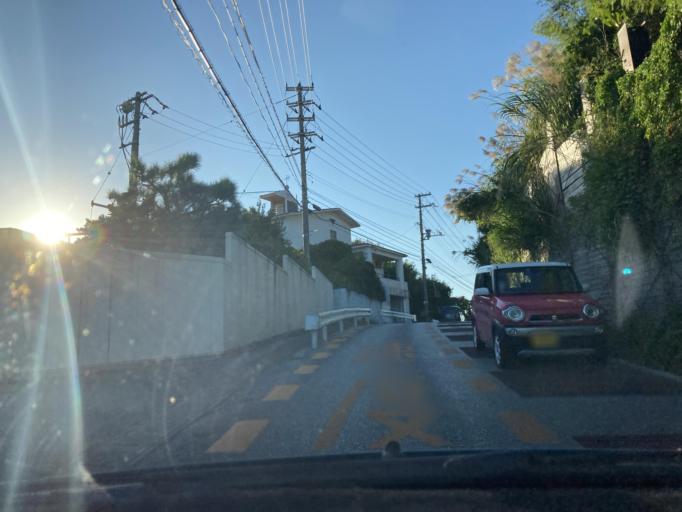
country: JP
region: Okinawa
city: Naha-shi
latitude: 26.2107
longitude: 127.7312
